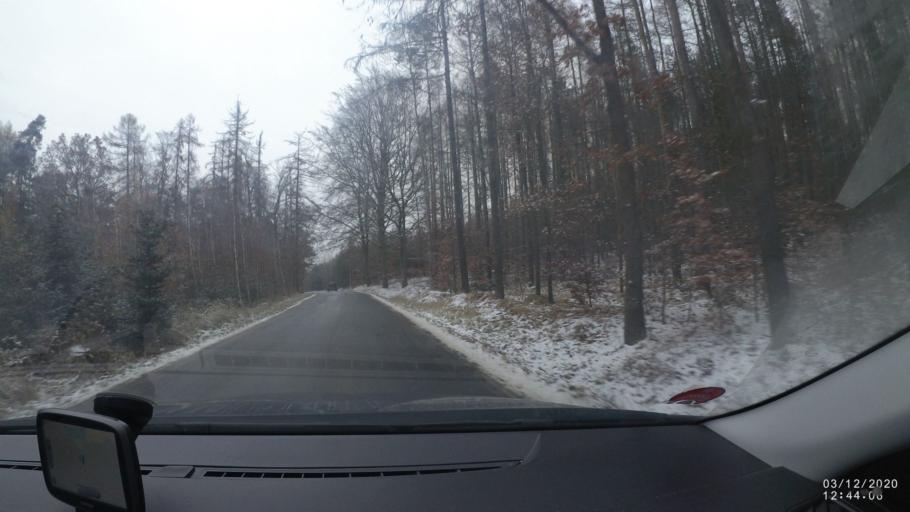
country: CZ
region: Central Bohemia
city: Revnicov
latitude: 50.1697
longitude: 13.8437
